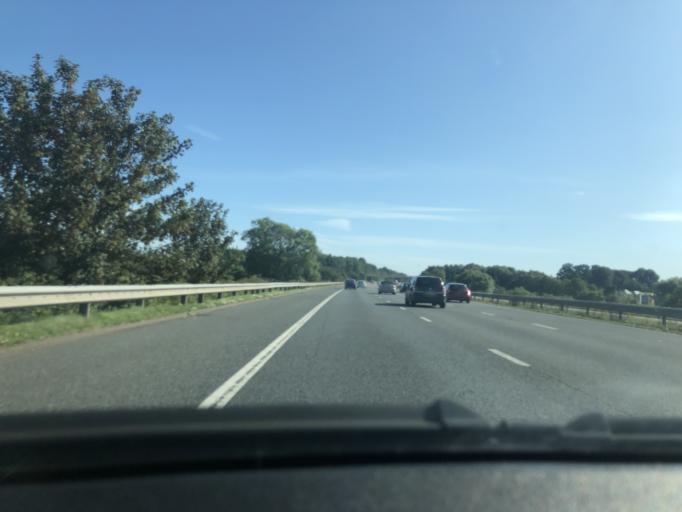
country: GB
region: England
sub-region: Devon
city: Heavitree
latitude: 50.7547
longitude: -3.4559
